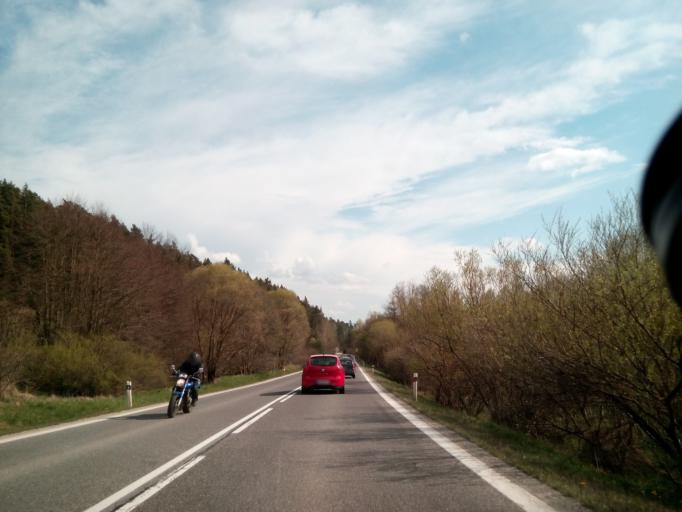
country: SK
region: Presovsky
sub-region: Okres Presov
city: Levoca
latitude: 49.0156
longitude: 20.6249
